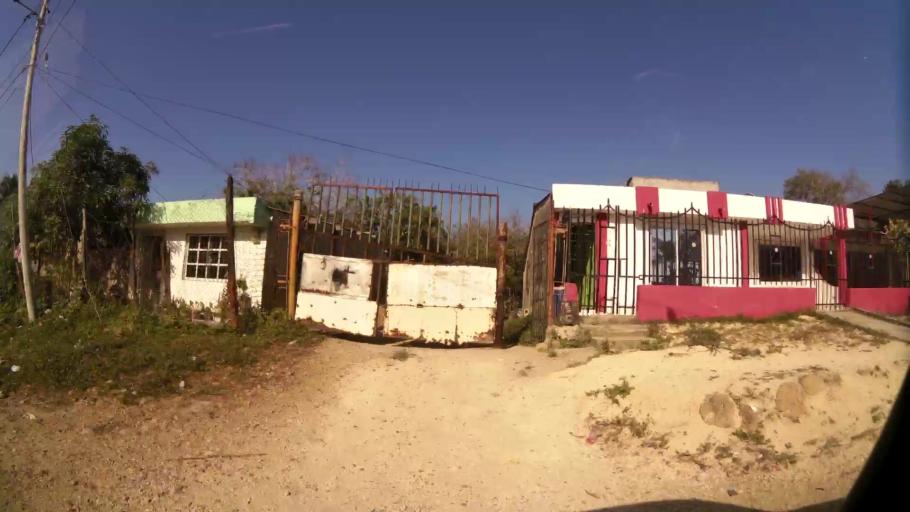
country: CO
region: Bolivar
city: Cartagena
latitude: 10.4027
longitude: -75.4802
